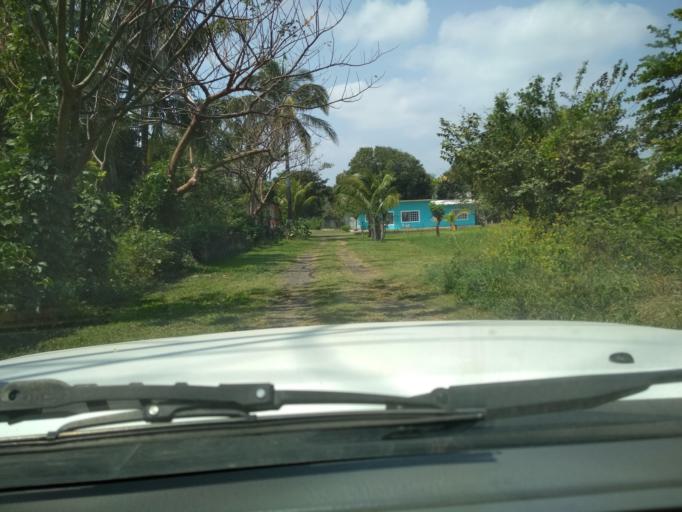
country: MX
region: Veracruz
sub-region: Medellin
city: Fraccionamiento Arboledas San Ramon
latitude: 19.0955
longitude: -96.1418
